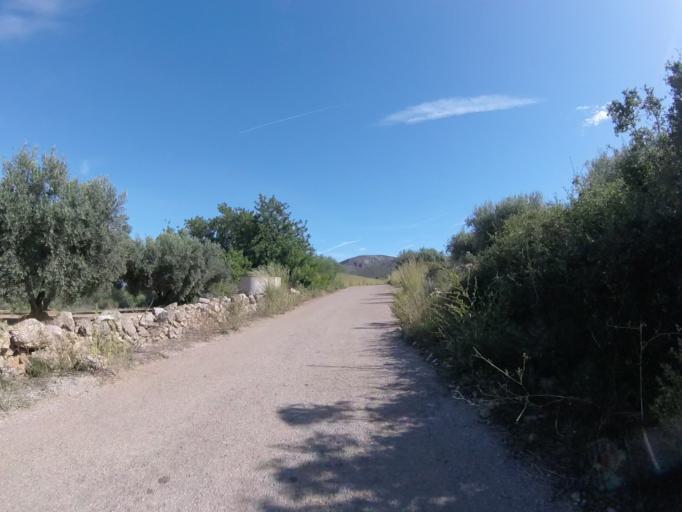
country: ES
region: Valencia
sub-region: Provincia de Castello
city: Santa Magdalena de Pulpis
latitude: 40.3610
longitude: 0.3150
